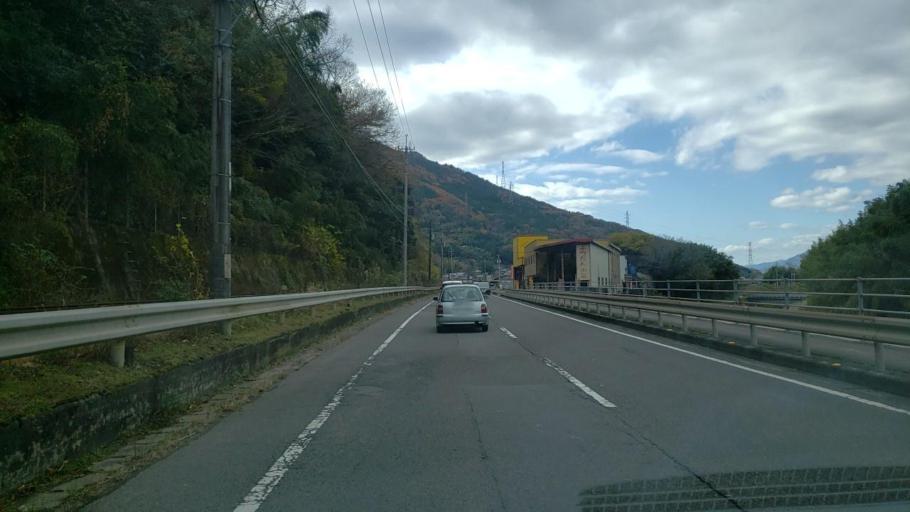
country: JP
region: Tokushima
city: Wakimachi
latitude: 34.0552
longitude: 134.1524
